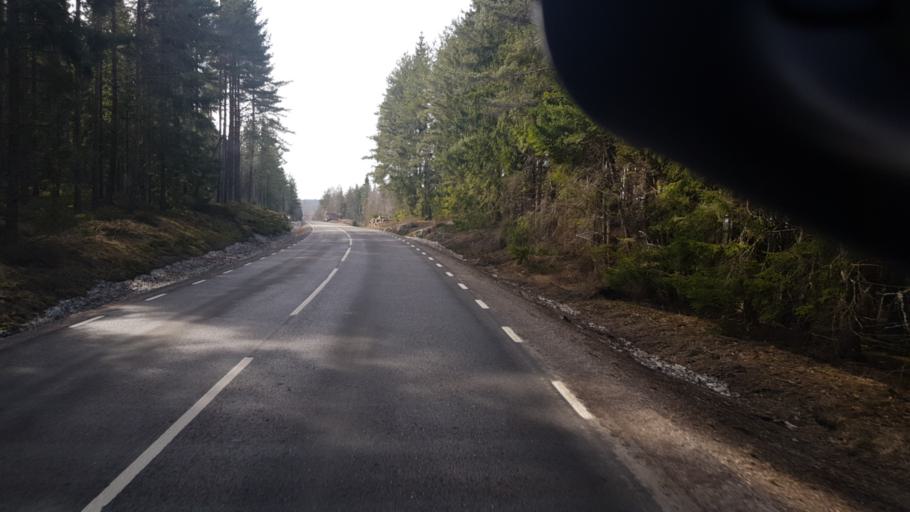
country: SE
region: Vaermland
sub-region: Eda Kommun
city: Amotfors
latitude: 59.7366
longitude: 12.4030
